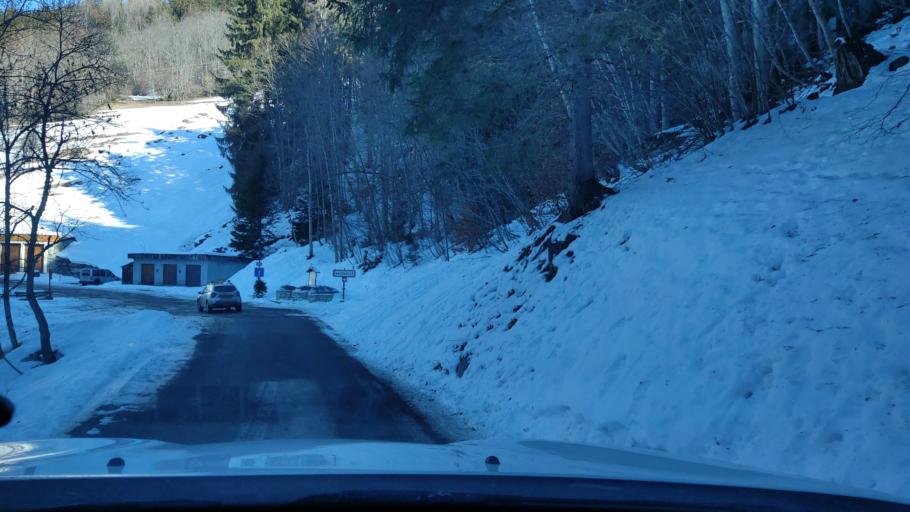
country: FR
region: Rhone-Alpes
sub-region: Departement de la Savoie
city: Les Allues
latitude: 45.4313
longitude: 6.5689
